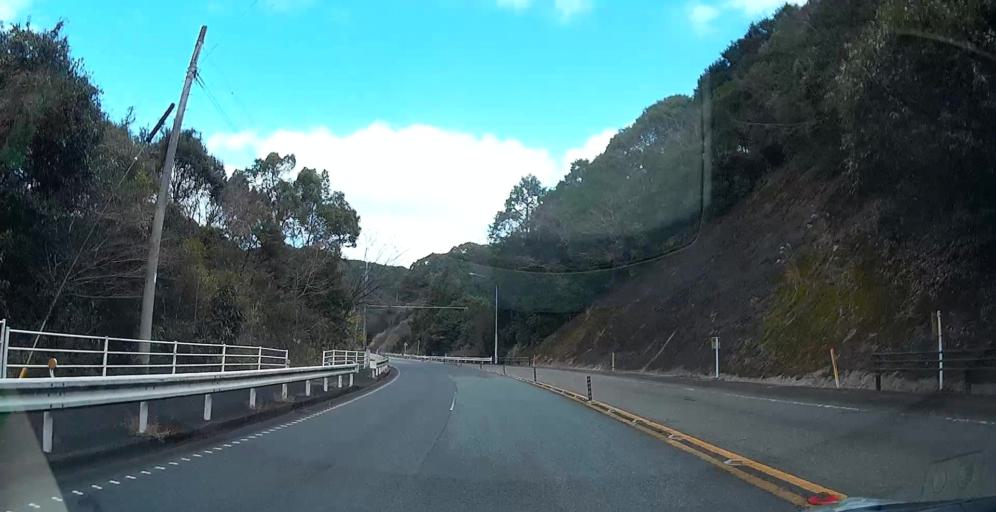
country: JP
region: Kumamoto
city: Yatsushiro
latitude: 32.3677
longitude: 130.5239
